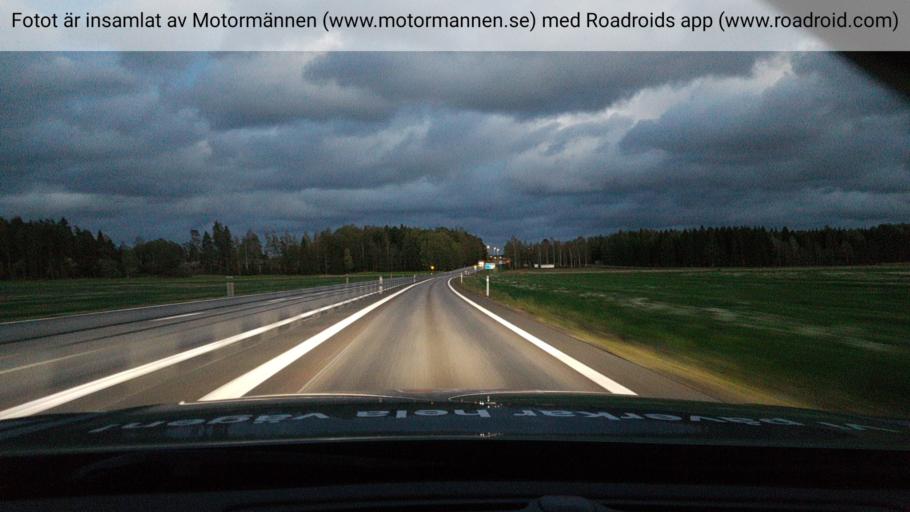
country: SE
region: Vaermland
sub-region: Kristinehamns Kommun
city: Kristinehamn
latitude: 59.3730
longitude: 14.0017
